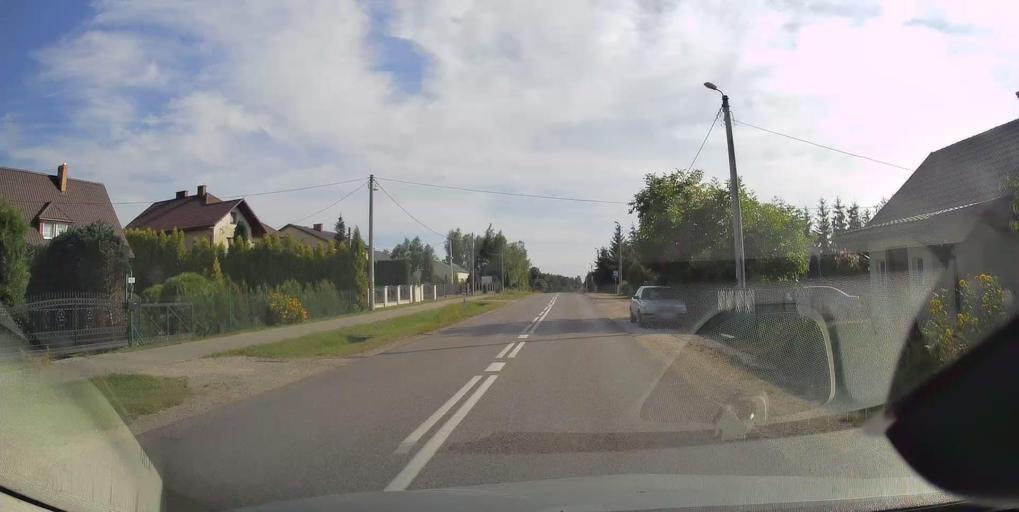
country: PL
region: Swietokrzyskie
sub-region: Powiat konecki
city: Radoszyce
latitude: 51.0839
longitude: 20.2867
